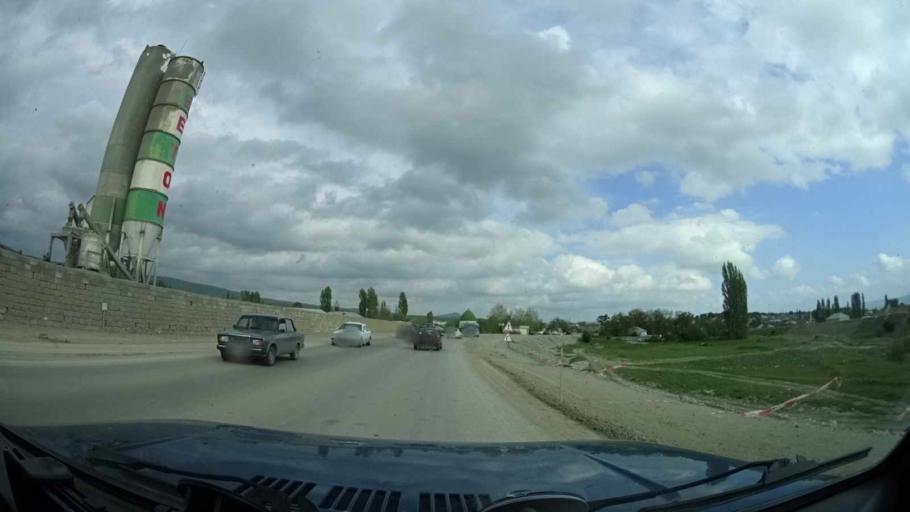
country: AZ
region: Samaxi
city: Shamakhi
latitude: 40.5953
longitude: 48.7005
